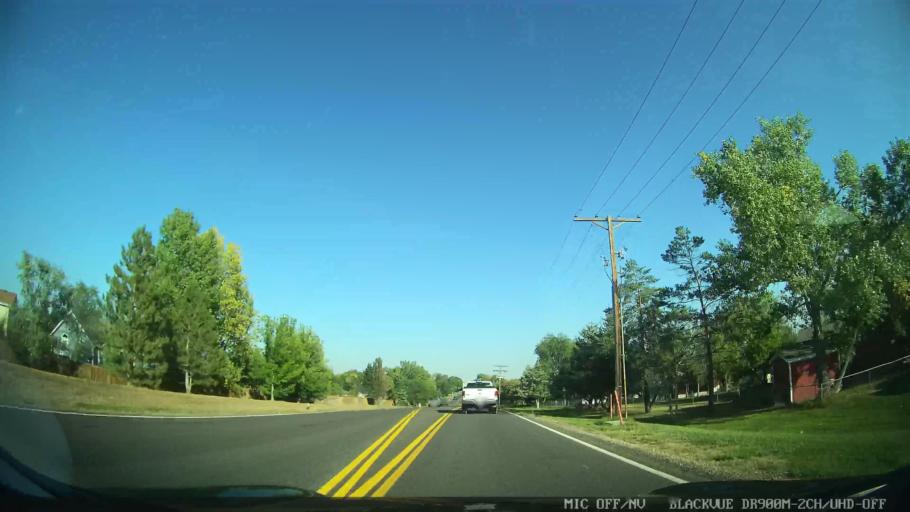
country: US
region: Colorado
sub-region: Larimer County
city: Loveland
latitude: 40.4510
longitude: -105.0719
